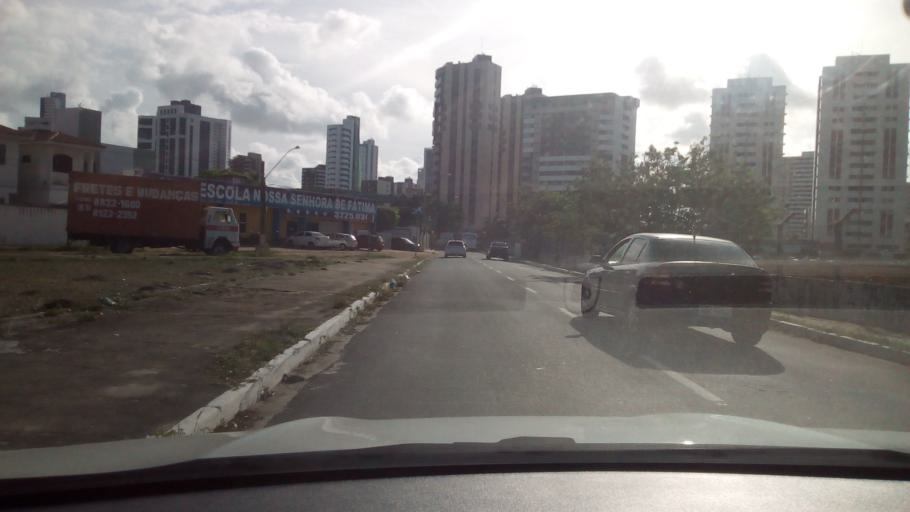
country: BR
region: Paraiba
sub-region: Joao Pessoa
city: Joao Pessoa
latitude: -7.0953
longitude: -34.8385
